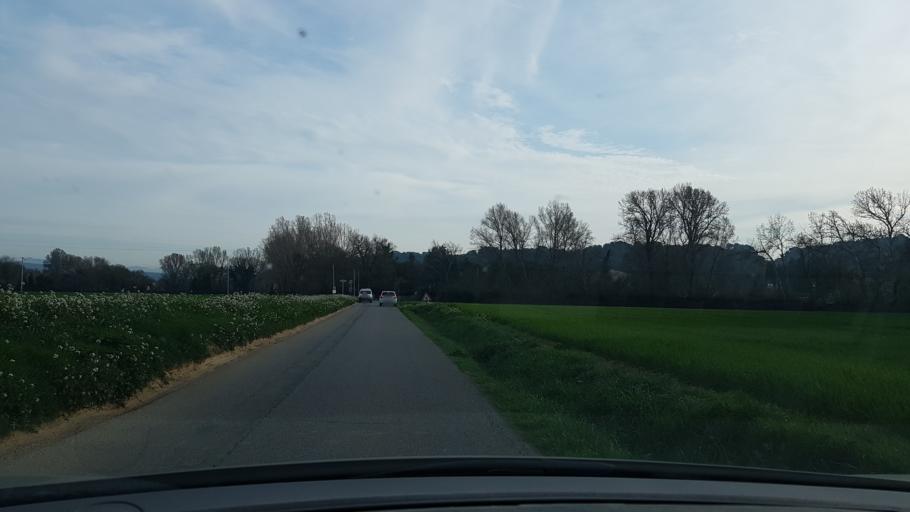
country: FR
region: Provence-Alpes-Cote d'Azur
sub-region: Departement des Bouches-du-Rhone
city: Bouc-Bel-Air
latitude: 43.5018
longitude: 5.4036
